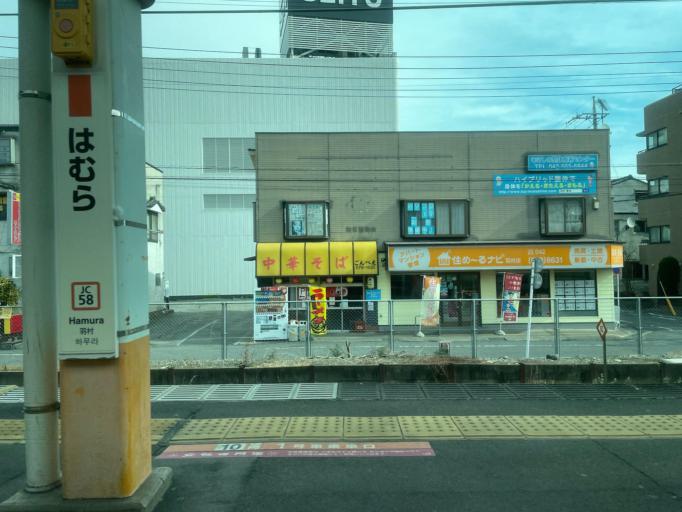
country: JP
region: Tokyo
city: Fussa
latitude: 35.7574
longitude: 139.3168
